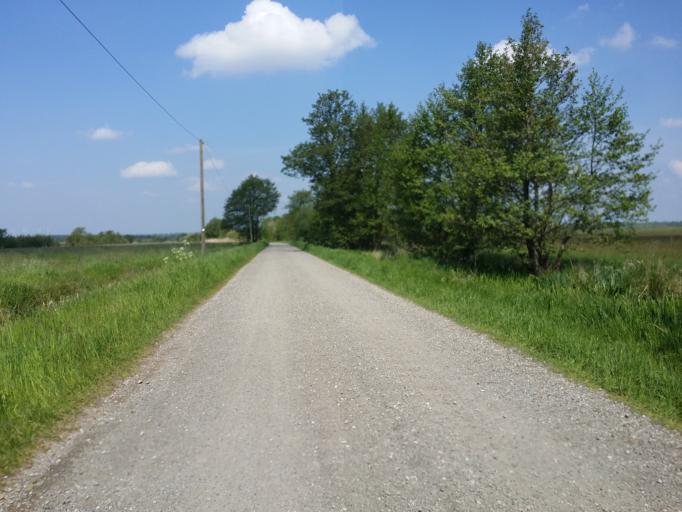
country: DE
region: Lower Saxony
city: Osterholz-Scharmbeck
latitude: 53.2173
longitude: 8.8556
